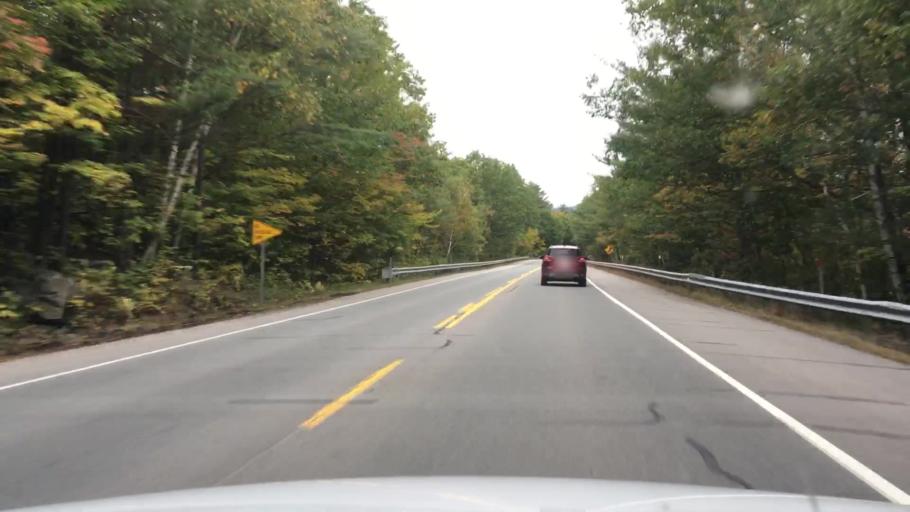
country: US
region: New Hampshire
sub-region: Coos County
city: Gorham
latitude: 44.3880
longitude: -71.0283
